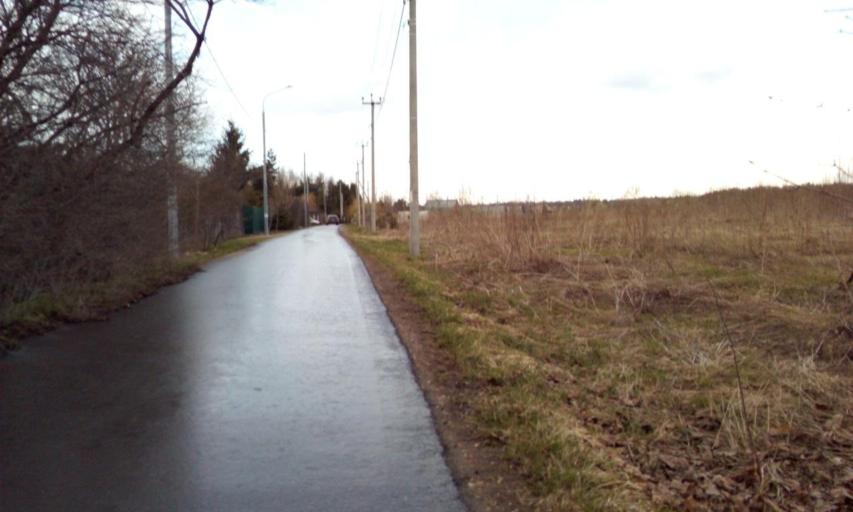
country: RU
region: Moskovskaya
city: Troitsk
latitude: 55.5213
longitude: 37.2649
